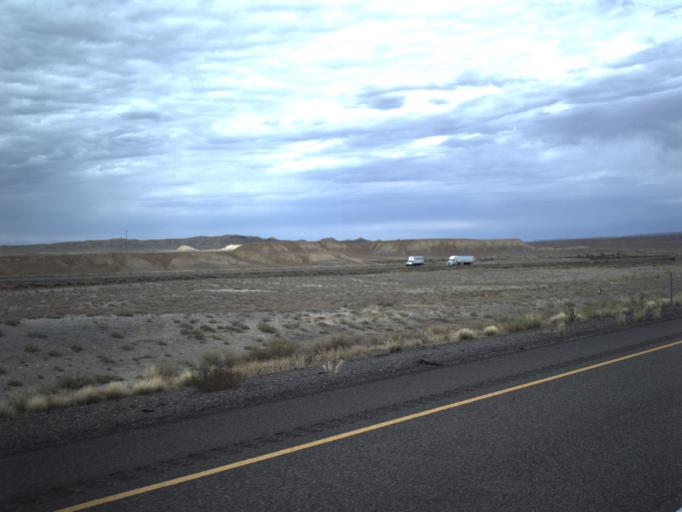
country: US
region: Utah
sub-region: Grand County
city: Moab
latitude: 38.9411
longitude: -109.5324
